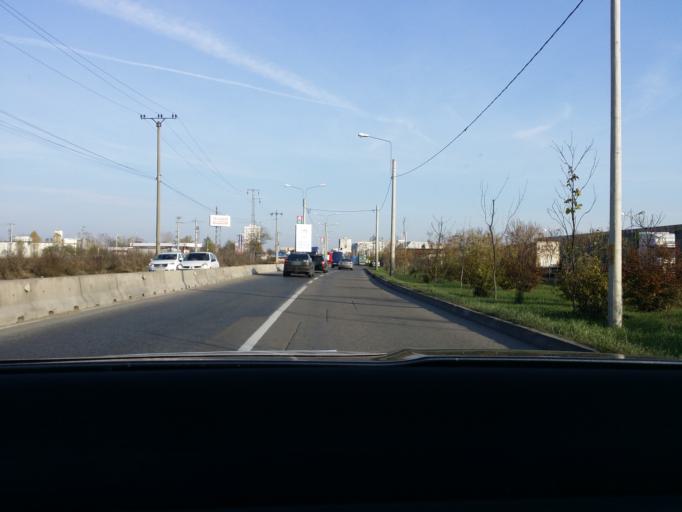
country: RO
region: Prahova
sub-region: Comuna Targsoru Vechi
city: Strejnicu
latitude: 44.9397
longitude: 25.9727
